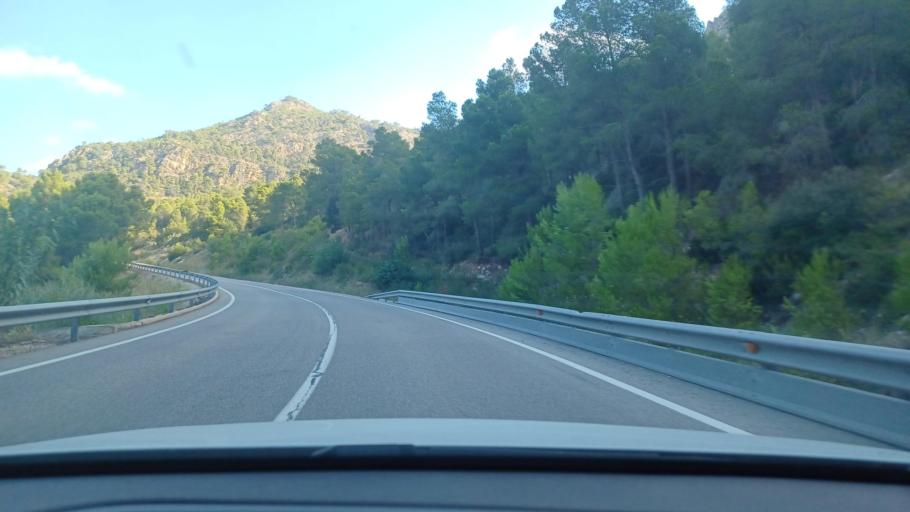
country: ES
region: Catalonia
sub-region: Provincia de Tarragona
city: Benifallet
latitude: 40.9615
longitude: 0.4479
